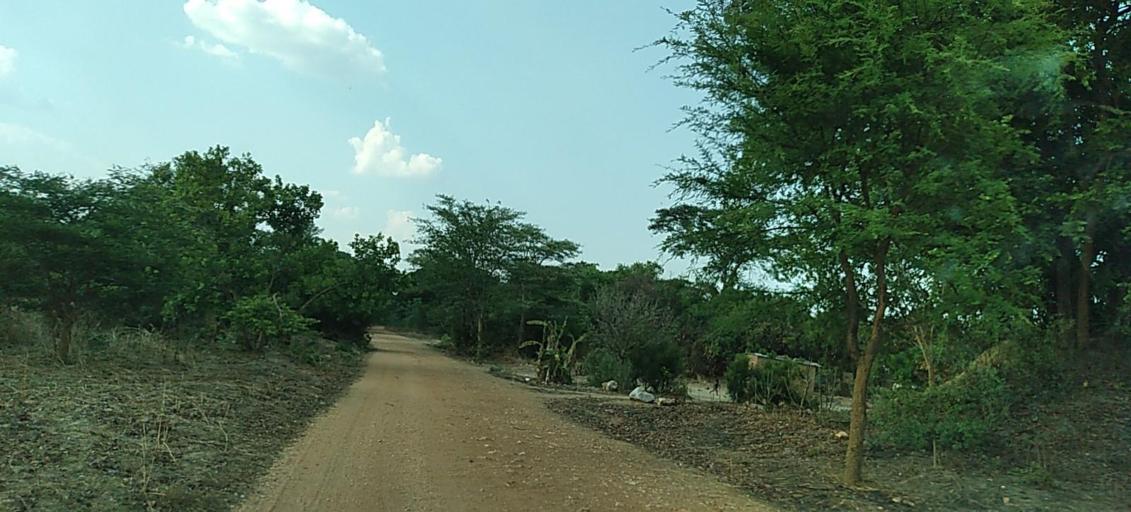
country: ZM
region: Copperbelt
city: Mpongwe
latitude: -13.4864
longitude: 28.0841
